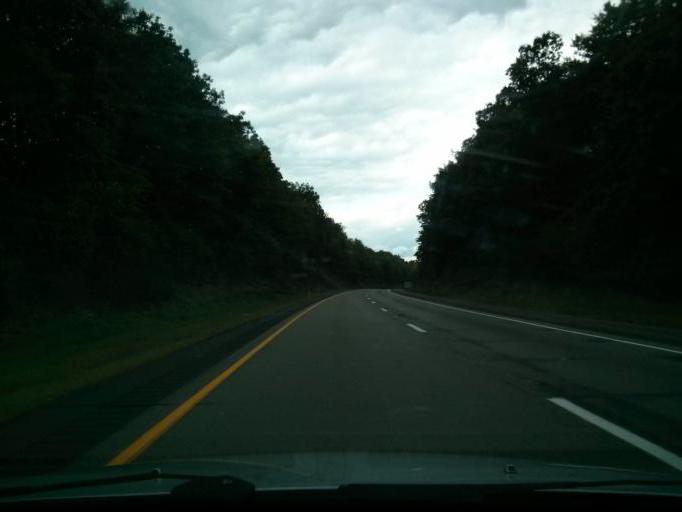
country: US
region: Pennsylvania
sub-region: Clarion County
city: Clarion
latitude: 41.1734
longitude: -79.2691
